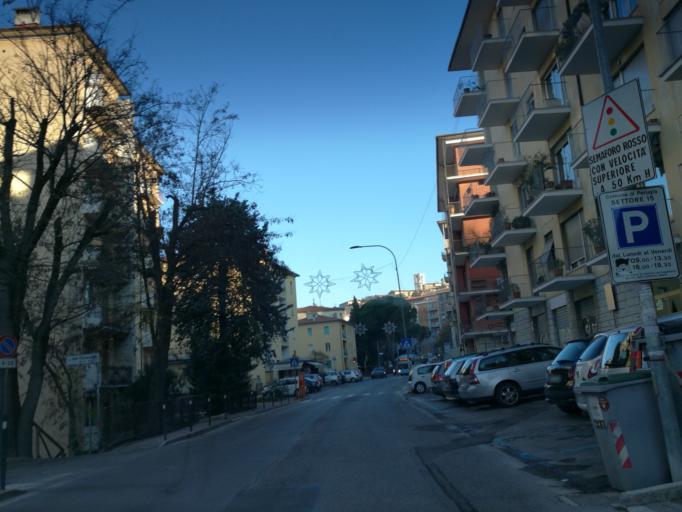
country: IT
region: Umbria
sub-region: Provincia di Perugia
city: Perugia
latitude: 43.0987
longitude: 12.3914
